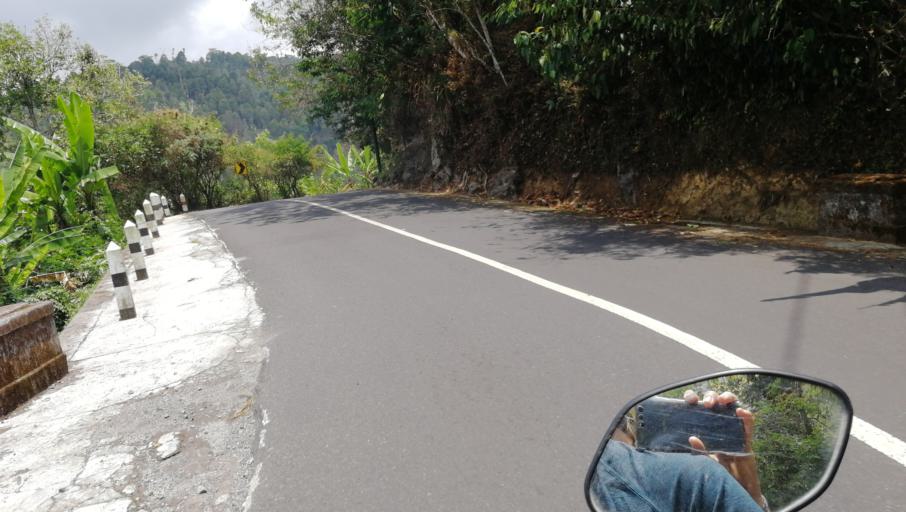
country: ID
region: Bali
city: Munduk
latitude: -8.2579
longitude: 115.0724
